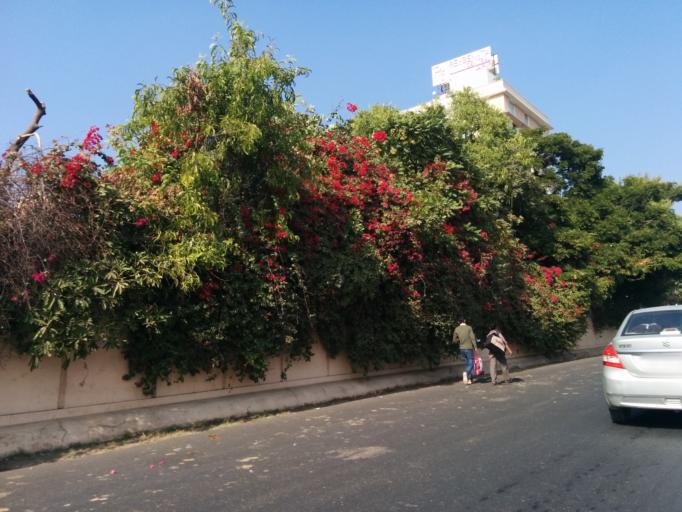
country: IN
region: Rajasthan
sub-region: Jaipur
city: Jaipur
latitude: 26.9575
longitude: 75.8436
